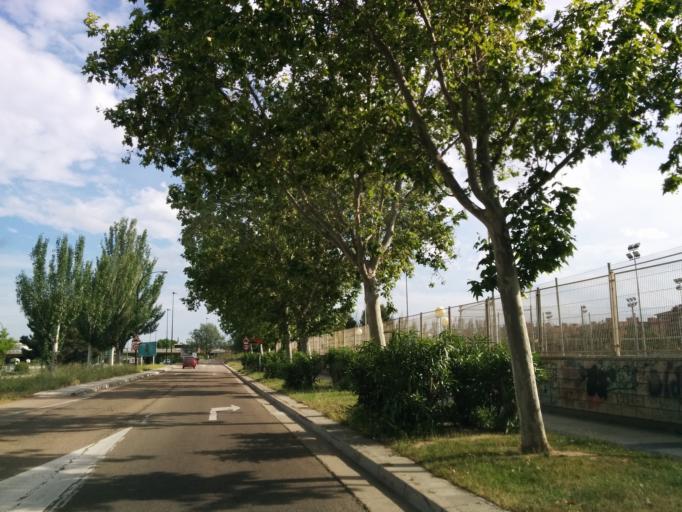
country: ES
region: Aragon
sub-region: Provincia de Zaragoza
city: Zaragoza
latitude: 41.6755
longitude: -0.8814
